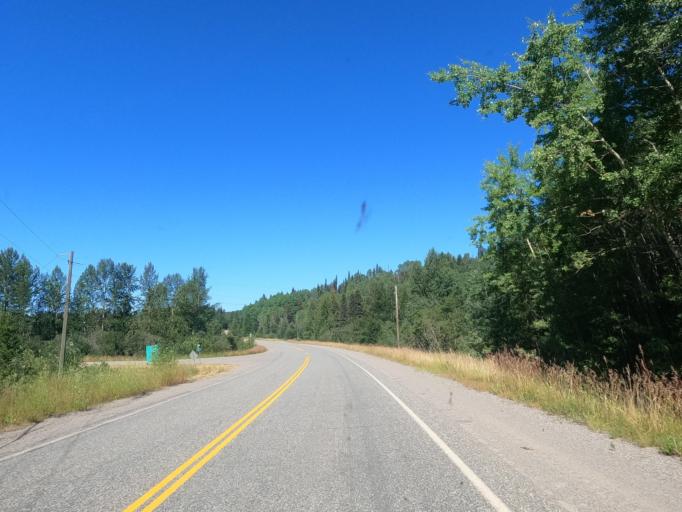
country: CA
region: British Columbia
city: Quesnel
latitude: 53.0526
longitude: -122.1564
